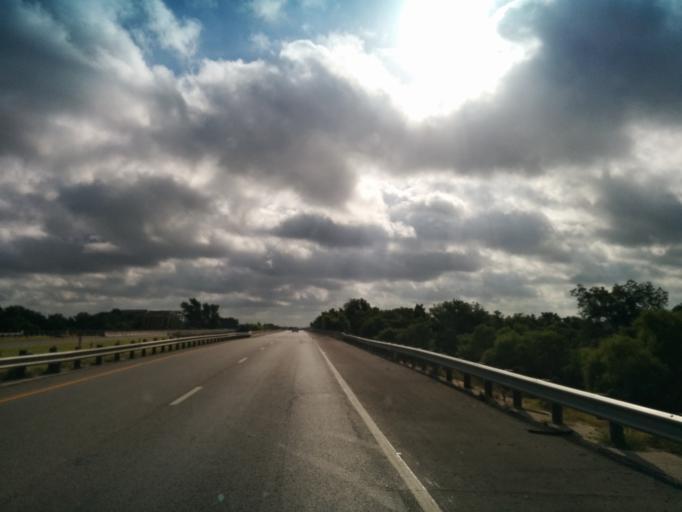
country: US
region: Texas
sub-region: Guadalupe County
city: Cibolo
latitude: 29.5003
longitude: -98.1882
